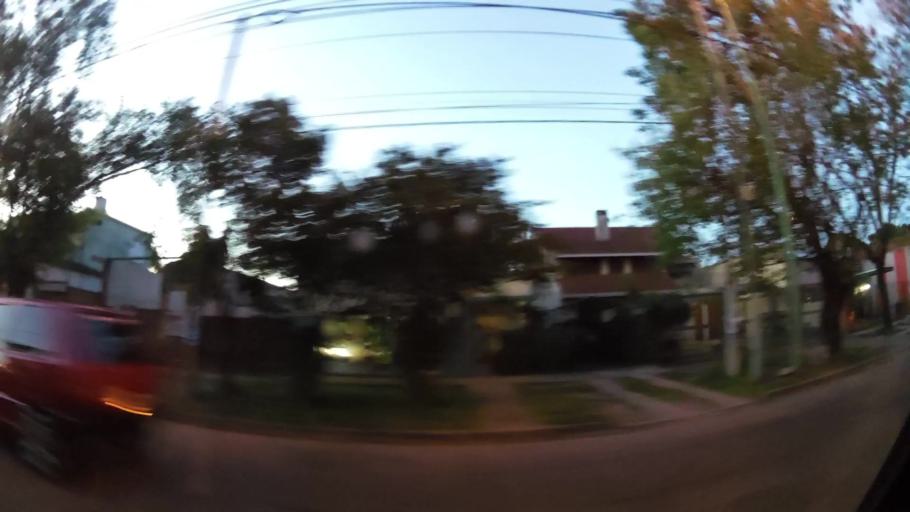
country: AR
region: Buenos Aires
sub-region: Partido de Quilmes
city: Quilmes
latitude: -34.7726
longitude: -58.2121
